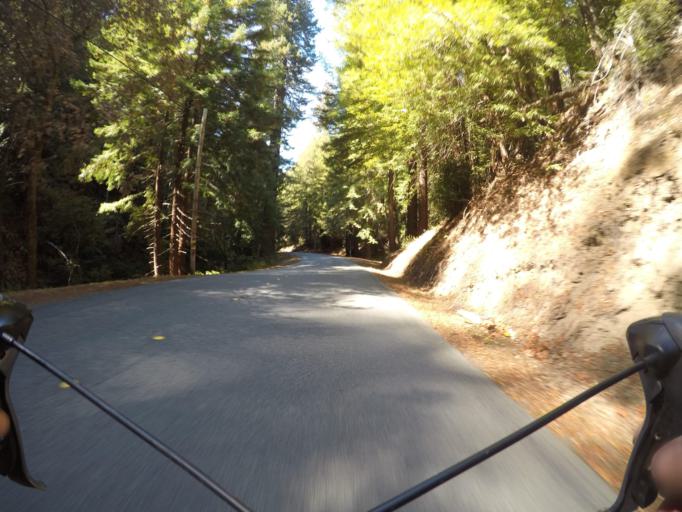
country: US
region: California
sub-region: San Mateo County
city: Portola Valley
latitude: 37.2976
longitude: -122.2505
